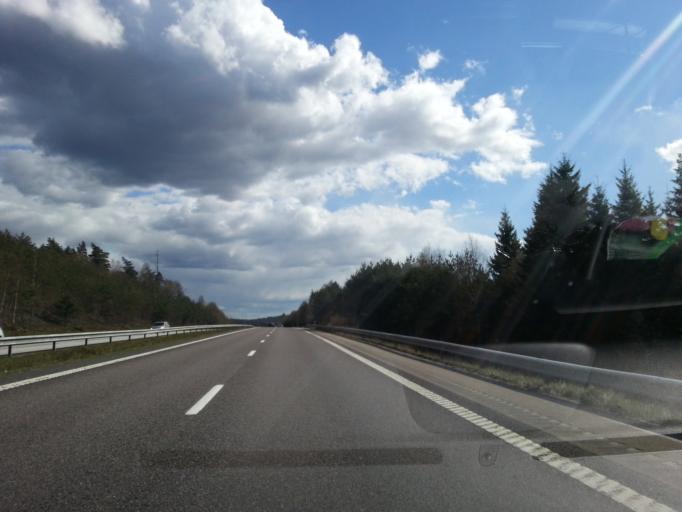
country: SE
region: Vaestra Goetaland
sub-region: Stenungsunds Kommun
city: Stenungsund
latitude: 58.0844
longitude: 11.8840
